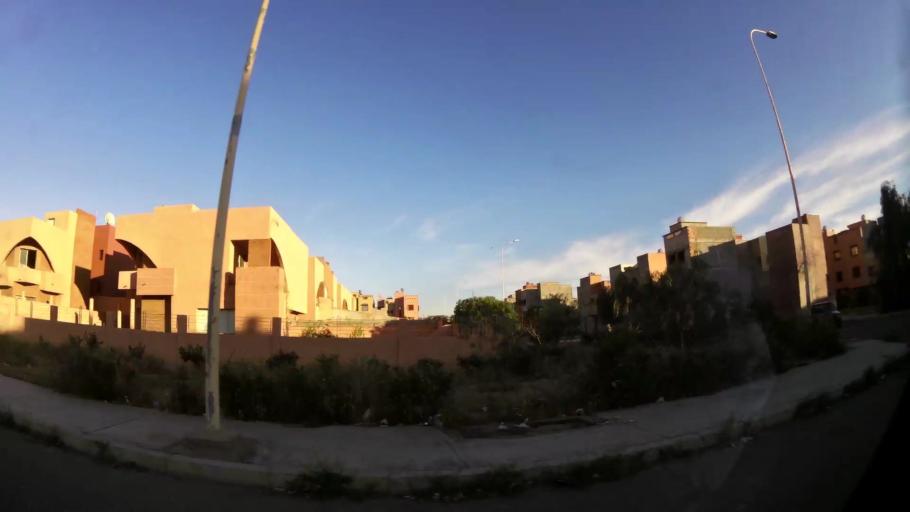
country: MA
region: Marrakech-Tensift-Al Haouz
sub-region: Marrakech
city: Marrakesh
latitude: 31.7468
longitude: -8.1090
